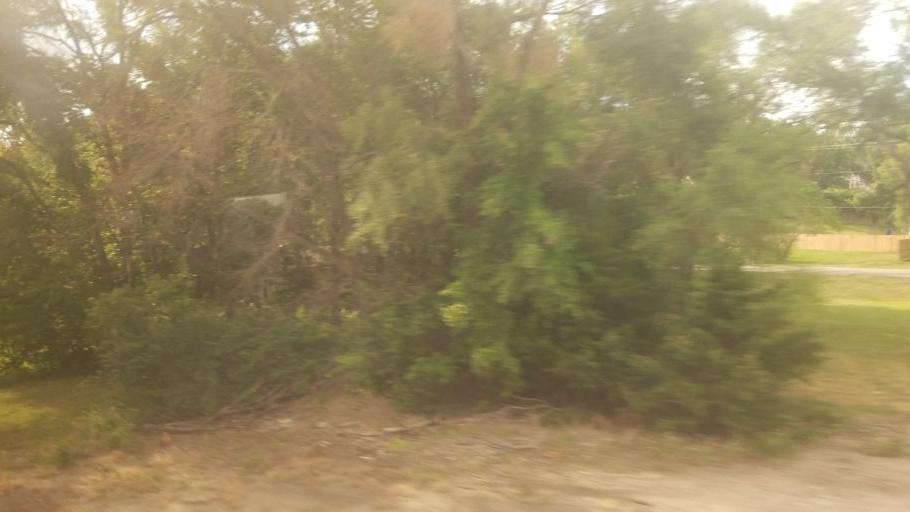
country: US
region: Kansas
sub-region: Douglas County
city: Eudora
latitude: 38.9487
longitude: -95.1002
